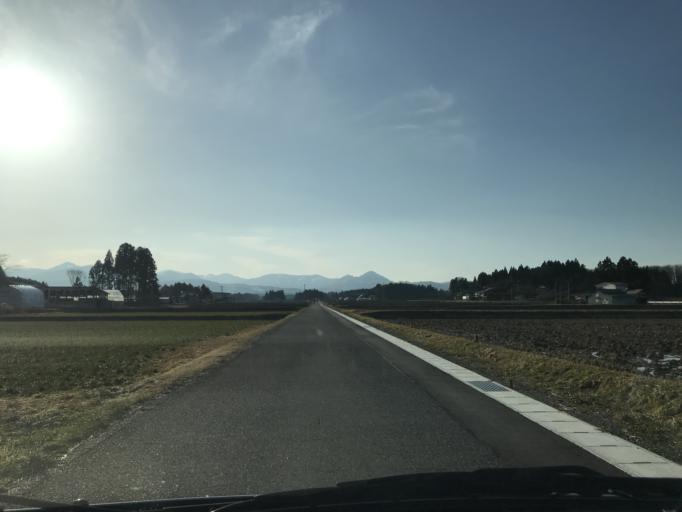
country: JP
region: Iwate
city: Kitakami
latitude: 39.2280
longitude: 141.0766
